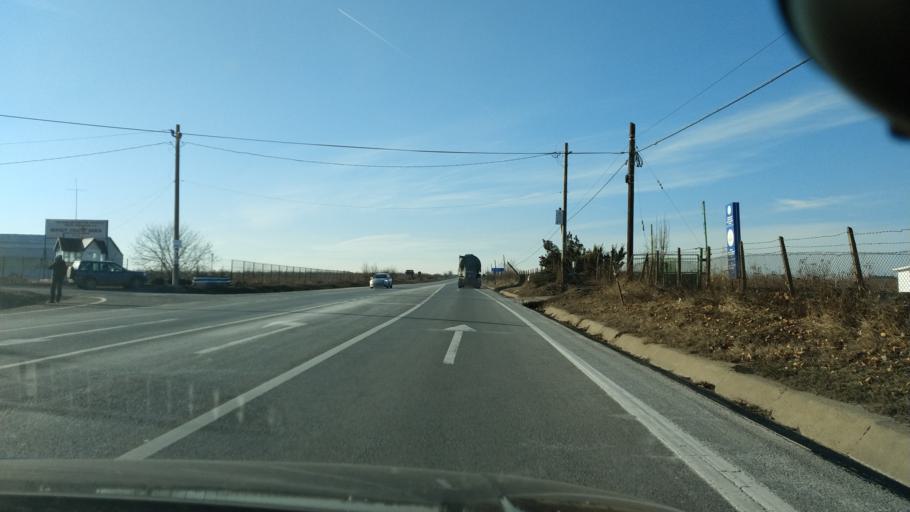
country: RO
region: Iasi
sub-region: Comuna Baltati
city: Baltati
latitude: 47.2220
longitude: 27.1460
